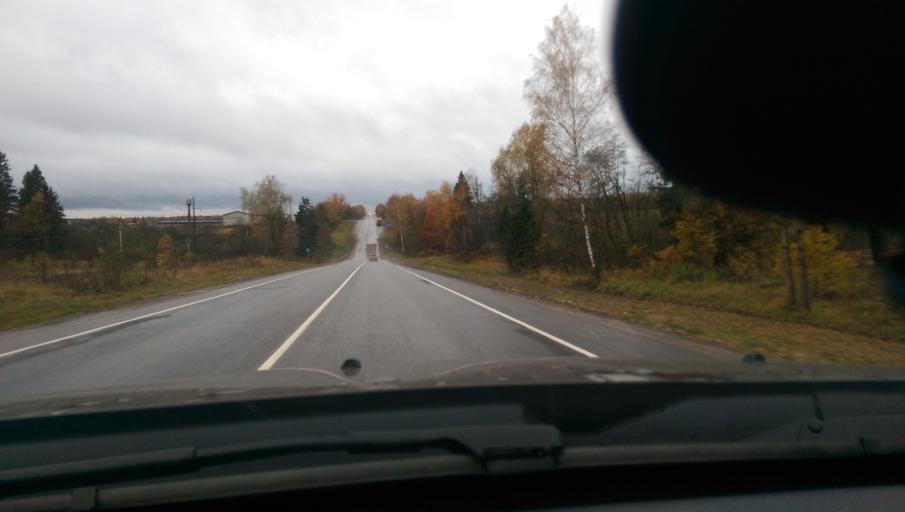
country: RU
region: Moskovskaya
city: Yel'digino
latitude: 56.1480
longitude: 37.8022
